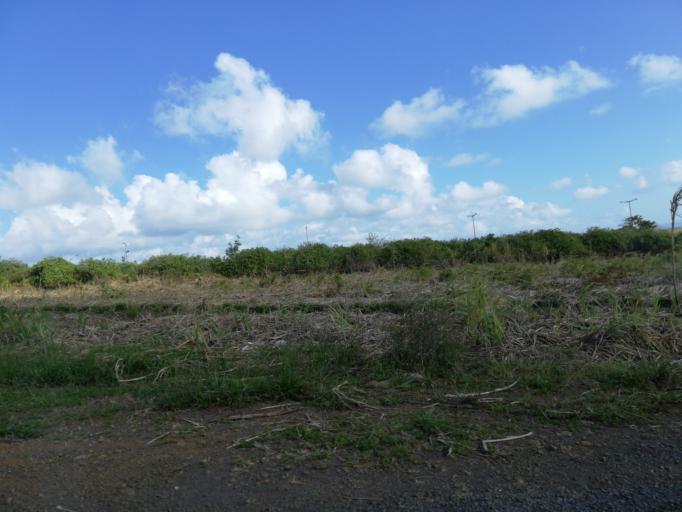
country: MU
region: Moka
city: Verdun
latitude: -20.2269
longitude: 57.5488
